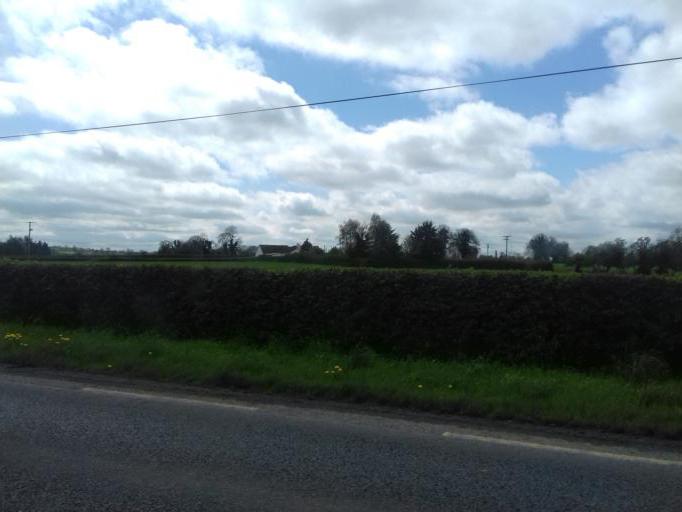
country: IE
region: Leinster
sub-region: Laois
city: Portlaoise
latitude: 53.0568
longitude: -7.3232
